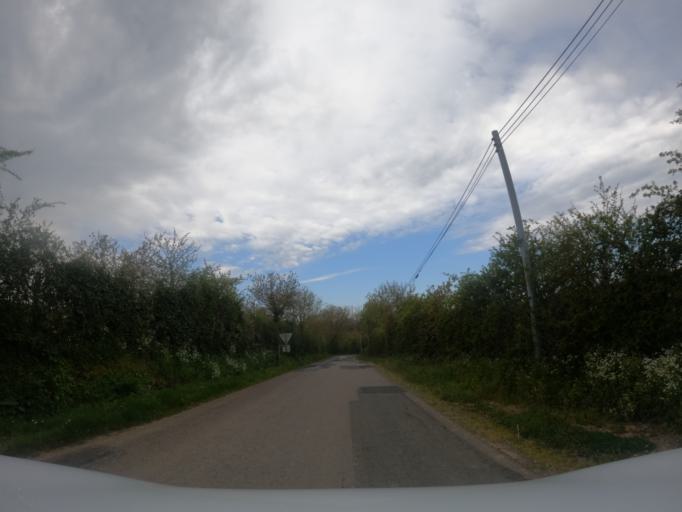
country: FR
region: Pays de la Loire
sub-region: Departement de la Vendee
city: Le Champ-Saint-Pere
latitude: 46.5277
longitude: -1.3275
